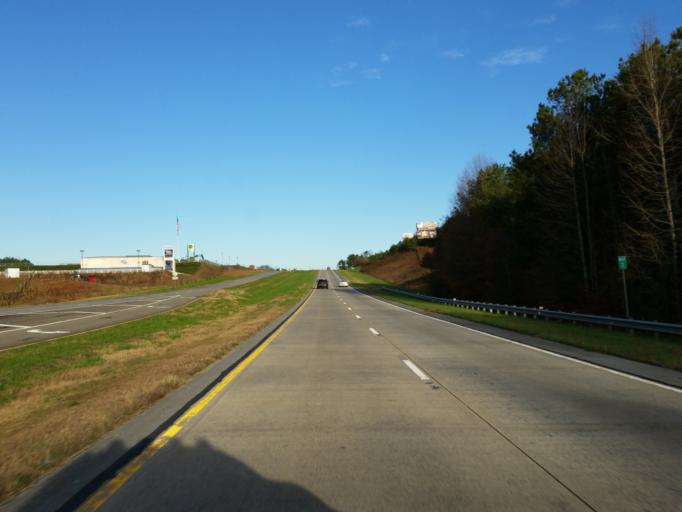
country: US
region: Georgia
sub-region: Pickens County
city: Nelson
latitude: 34.4016
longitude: -84.4169
